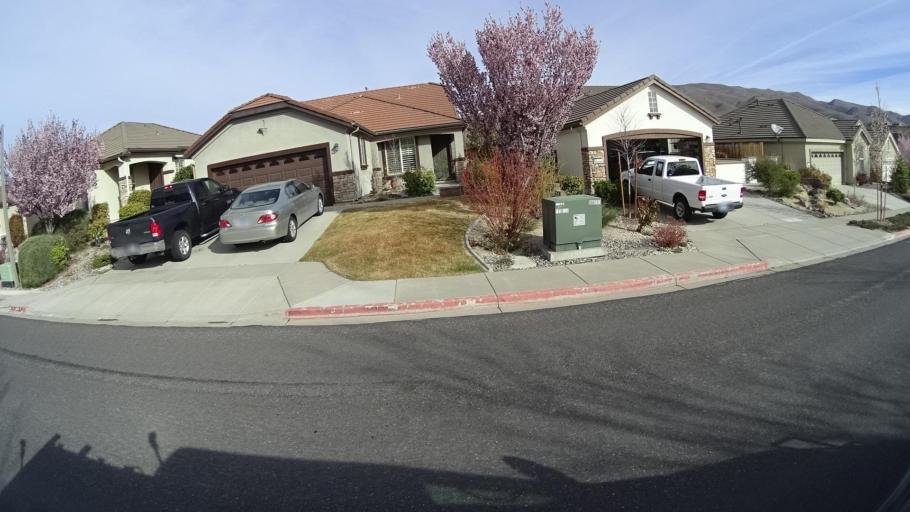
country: US
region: Nevada
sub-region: Washoe County
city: Mogul
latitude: 39.5208
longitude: -119.9500
